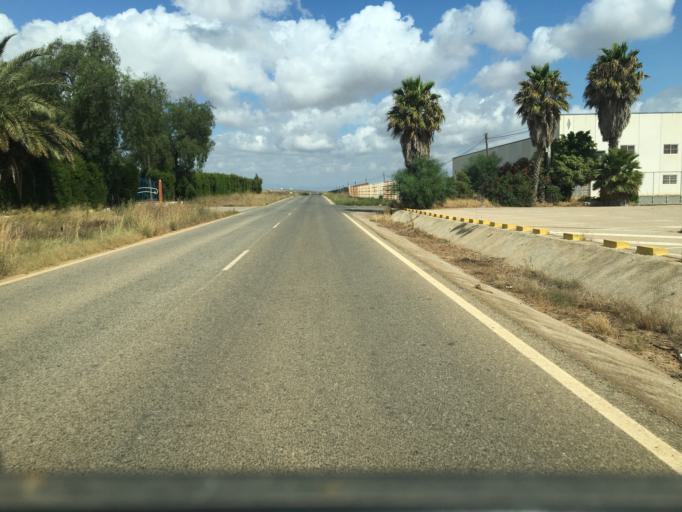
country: ES
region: Murcia
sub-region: Murcia
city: La Union
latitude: 37.6474
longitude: -0.8763
